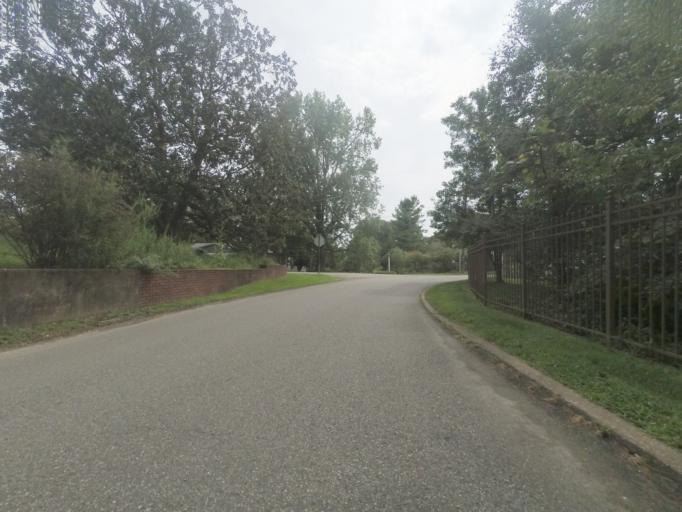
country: US
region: West Virginia
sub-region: Cabell County
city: Huntington
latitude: 38.3965
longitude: -82.4379
